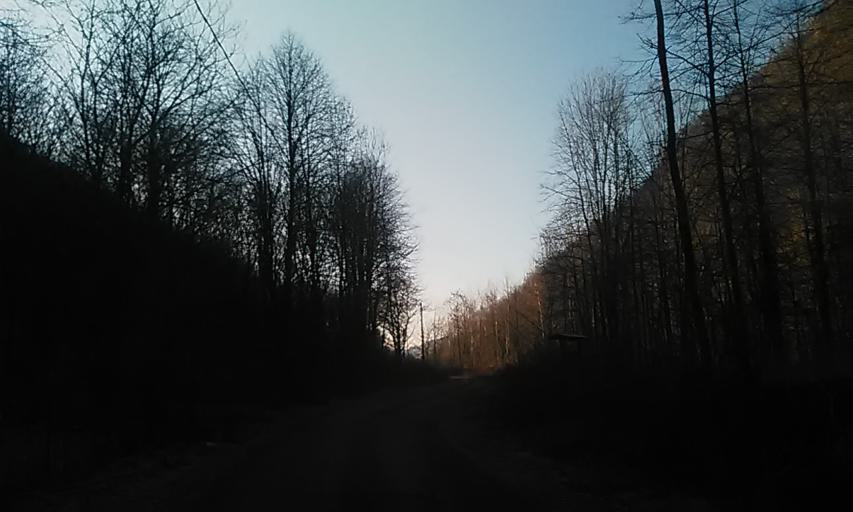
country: IT
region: Piedmont
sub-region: Provincia di Vercelli
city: Quarona
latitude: 45.7708
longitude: 8.2736
